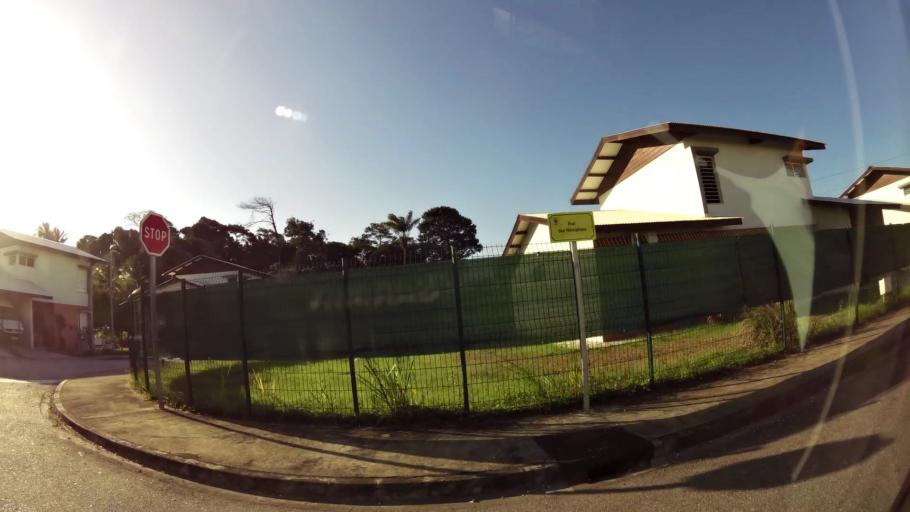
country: GF
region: Guyane
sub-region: Guyane
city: Remire-Montjoly
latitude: 4.8904
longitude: -52.2896
